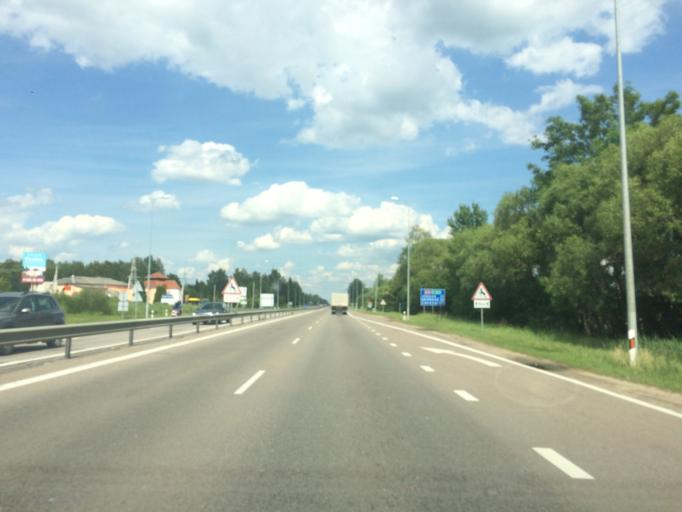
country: LT
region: Kauno apskritis
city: Dainava (Kaunas)
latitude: 54.9360
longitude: 23.9895
